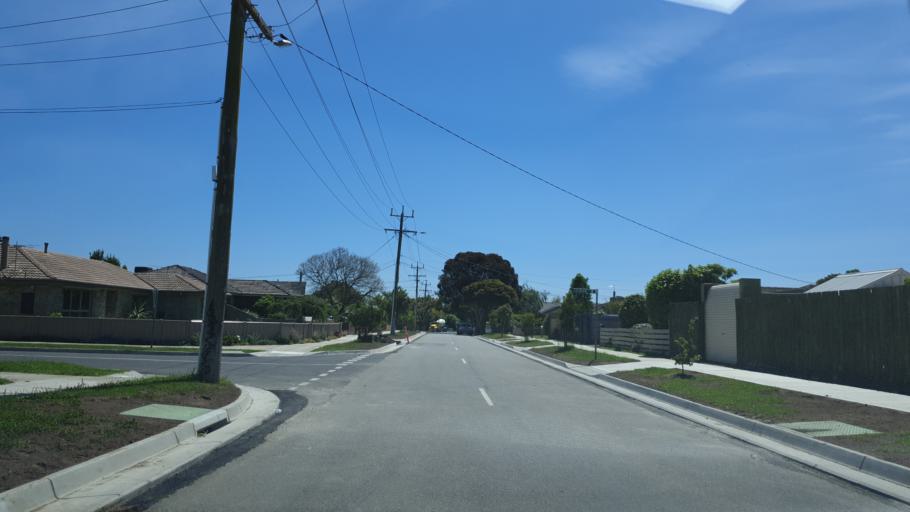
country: AU
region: Victoria
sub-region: Casey
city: Cranbourne
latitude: -38.1072
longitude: 145.2798
